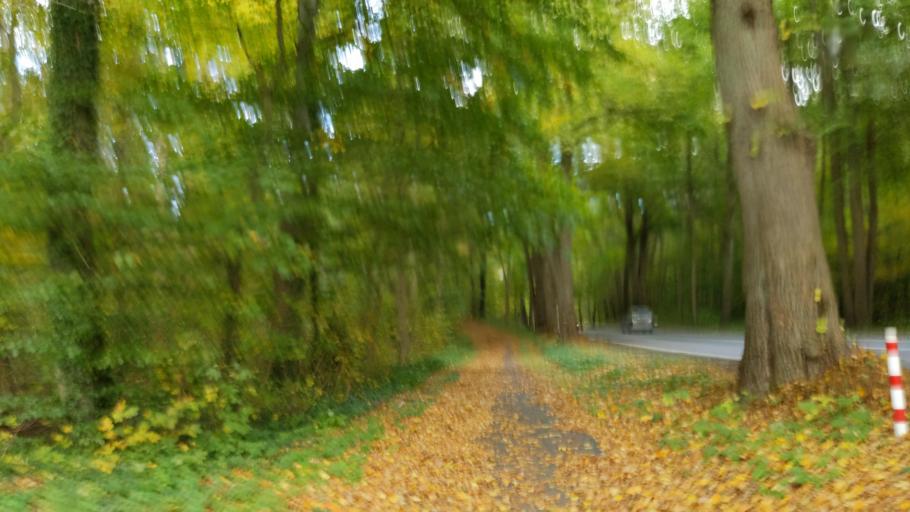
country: DE
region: Schleswig-Holstein
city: Kasseedorf
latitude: 54.1467
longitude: 10.6837
